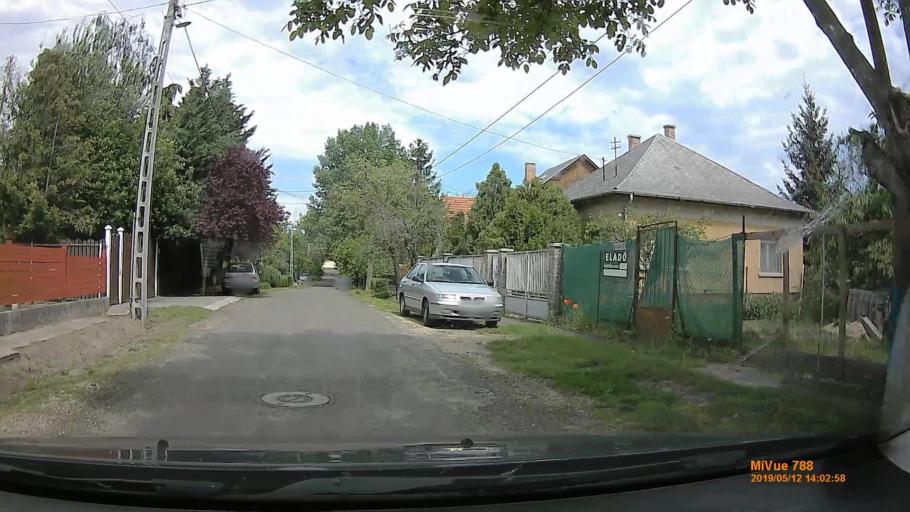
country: HU
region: Budapest
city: Budapest XVII. keruelet
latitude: 47.4899
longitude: 19.2951
